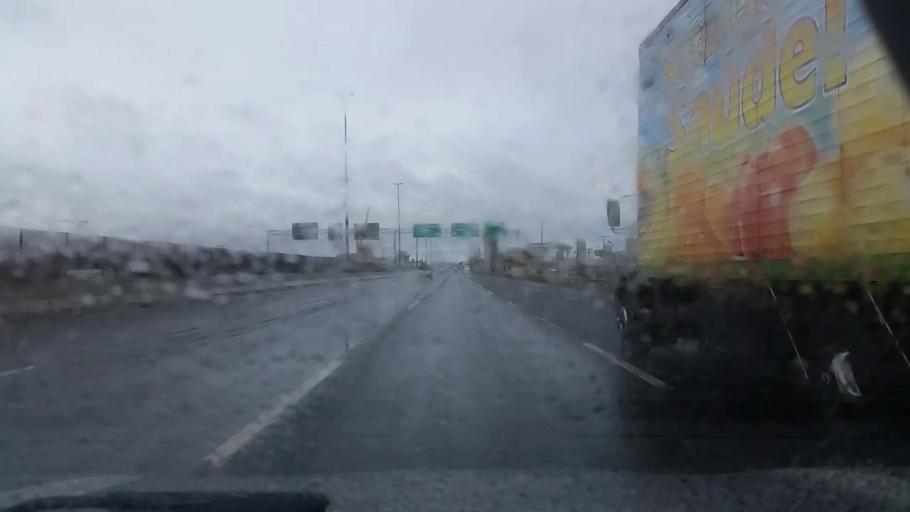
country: BR
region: Rio Grande do Sul
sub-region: Porto Alegre
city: Porto Alegre
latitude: -29.9832
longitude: -51.2020
